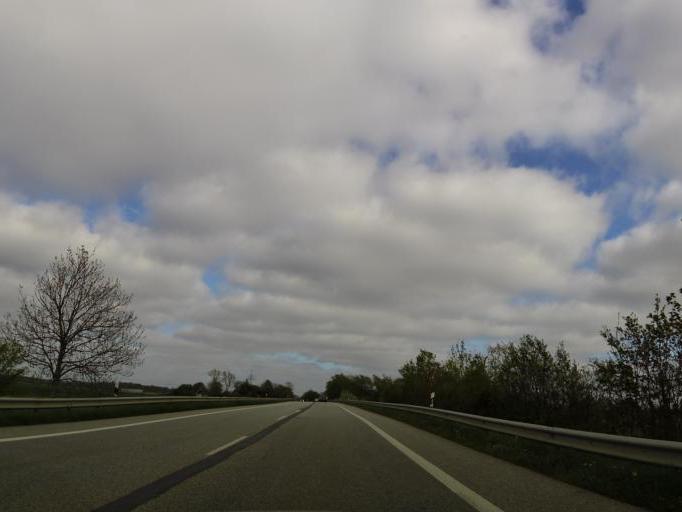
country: DE
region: Schleswig-Holstein
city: Risum-Lindholm
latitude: 54.7545
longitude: 8.8935
